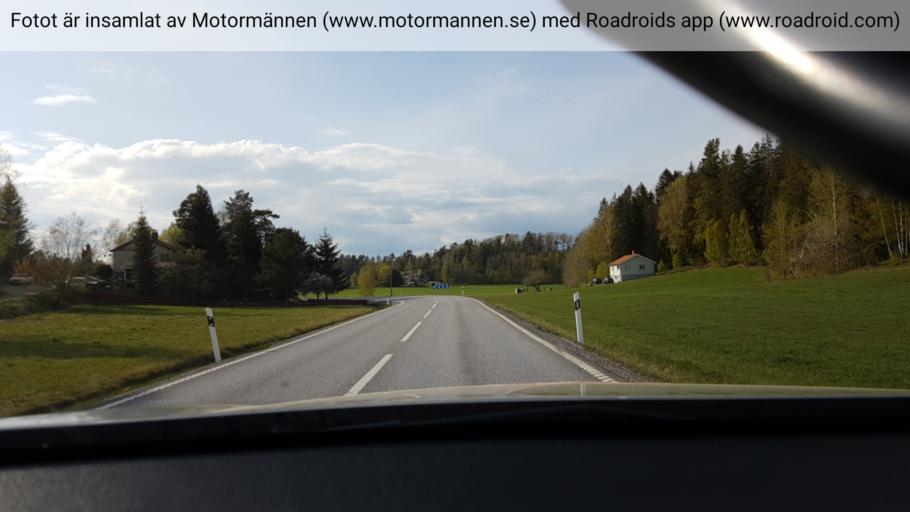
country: SE
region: Stockholm
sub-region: Nynashamns Kommun
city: Osmo
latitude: 58.9949
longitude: 17.8084
